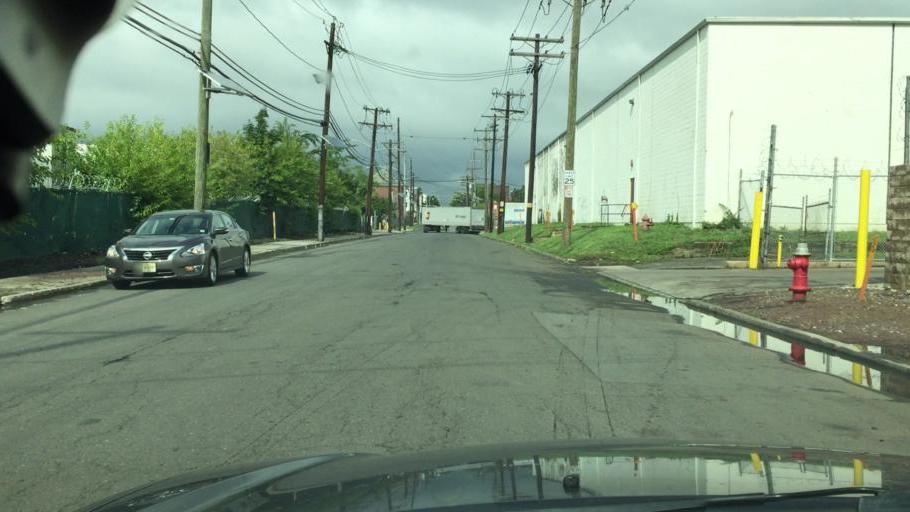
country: US
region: New Jersey
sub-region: Union County
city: Elizabeth
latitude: 40.6450
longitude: -74.1935
